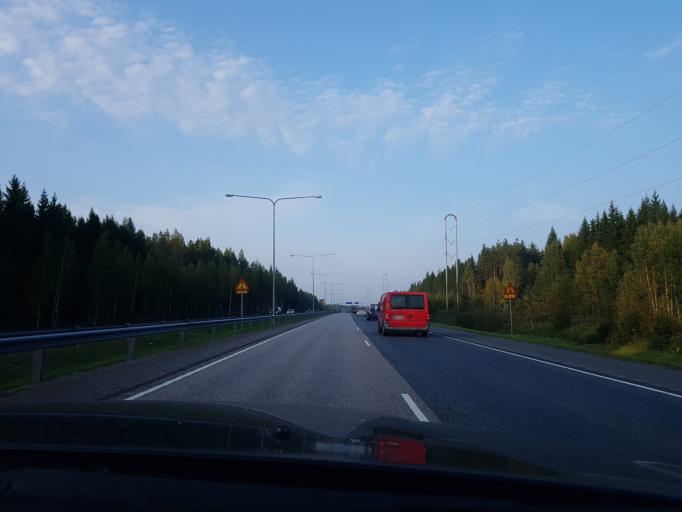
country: FI
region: Uusimaa
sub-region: Helsinki
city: Tuusula
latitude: 60.3622
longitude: 25.0032
